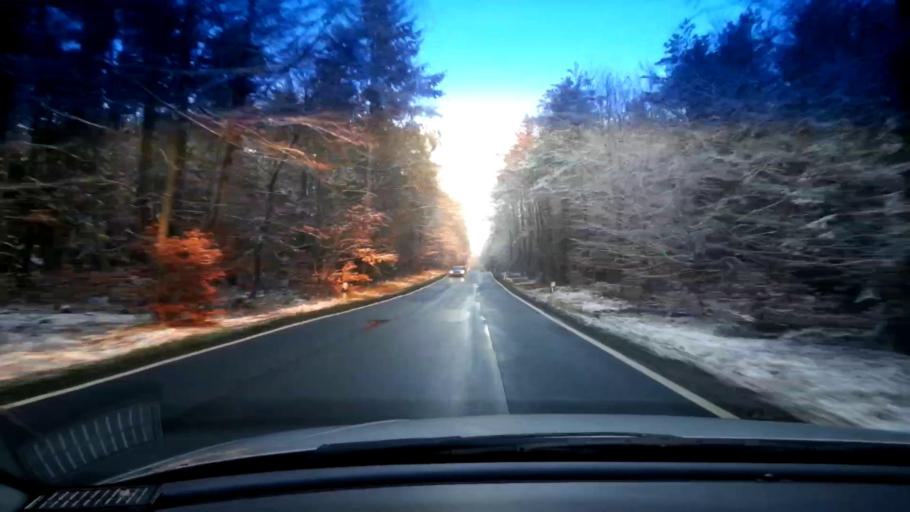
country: DE
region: Bavaria
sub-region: Upper Franconia
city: Pommersfelden
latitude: 49.7501
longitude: 10.8601
